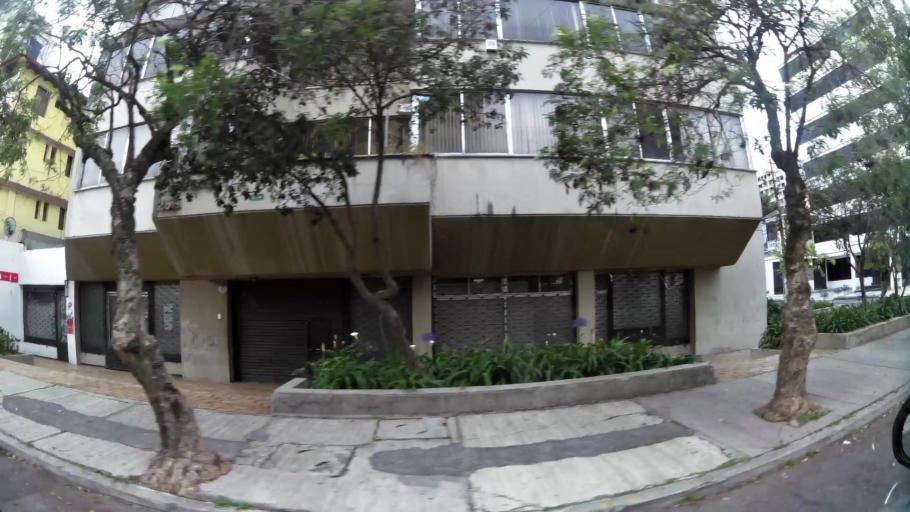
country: EC
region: Pichincha
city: Quito
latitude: -0.1994
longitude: -78.4886
